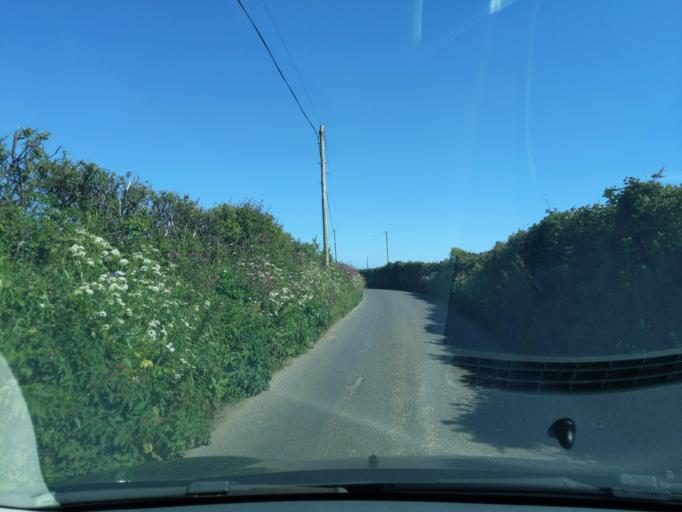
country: GB
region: England
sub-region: Cornwall
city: St. Buryan
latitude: 50.0698
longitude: -5.6107
